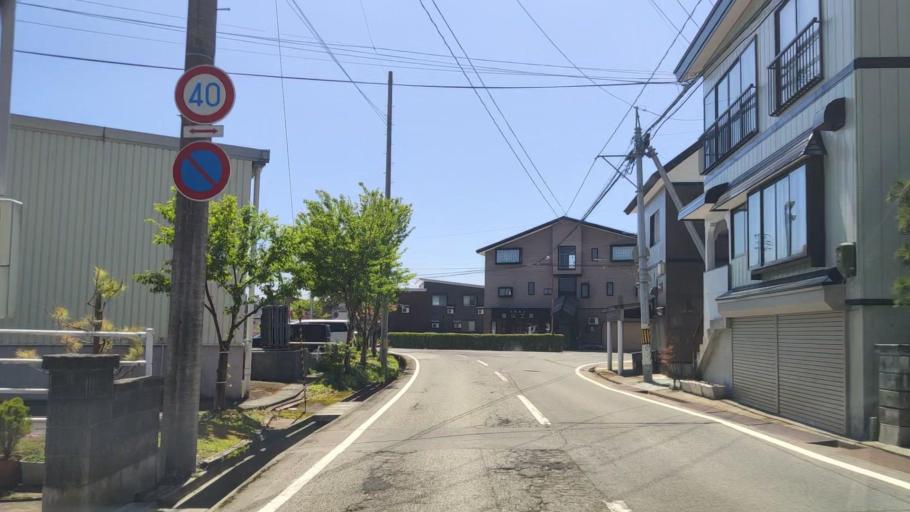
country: JP
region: Yamagata
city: Shinjo
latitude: 38.7731
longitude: 140.3079
